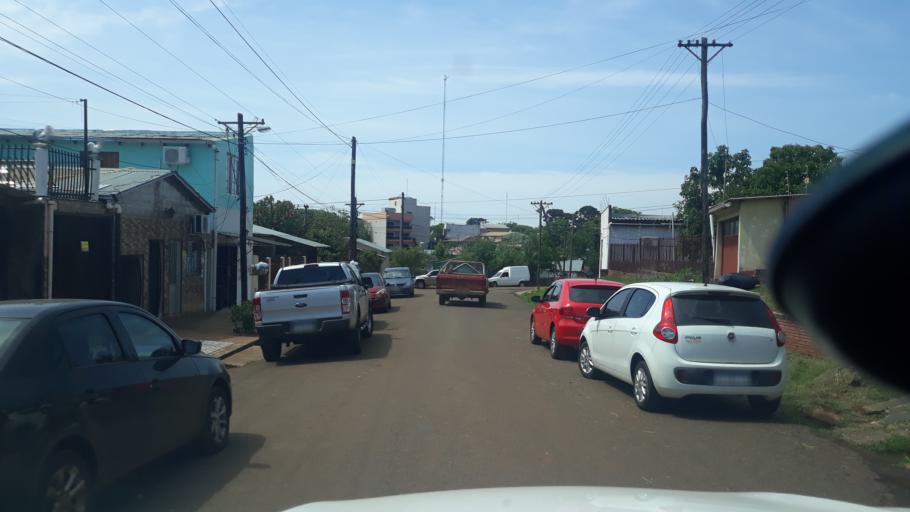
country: AR
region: Misiones
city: Bernardo de Irigoyen
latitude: -26.2537
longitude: -53.6488
